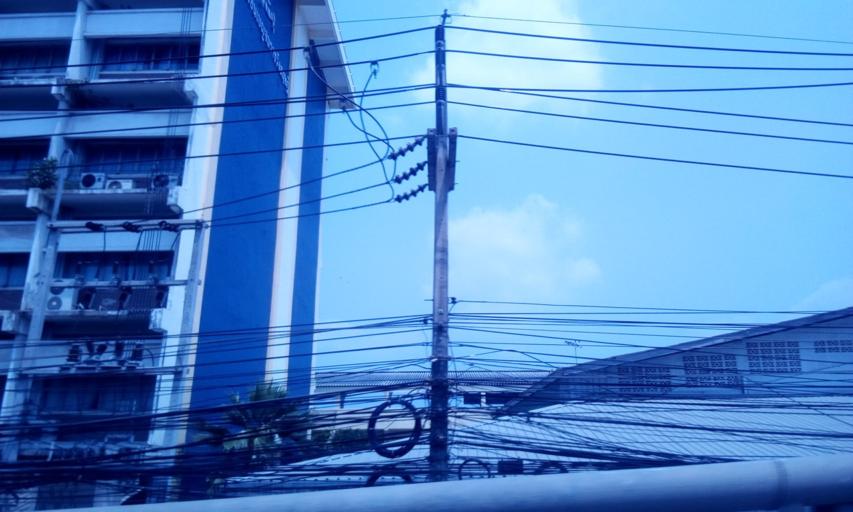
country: TH
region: Chachoengsao
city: Chachoengsao
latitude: 13.6905
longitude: 101.0757
